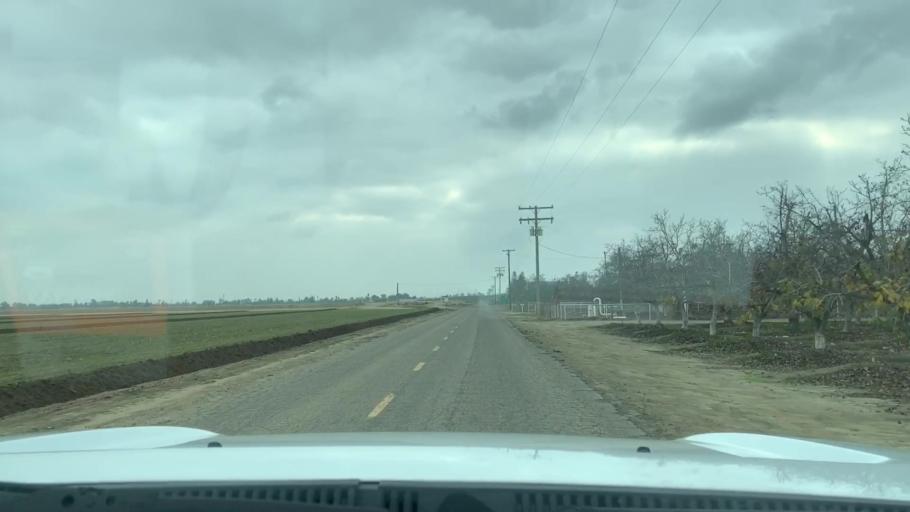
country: US
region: California
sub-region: Tulare County
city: Goshen
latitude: 36.3654
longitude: -119.4214
